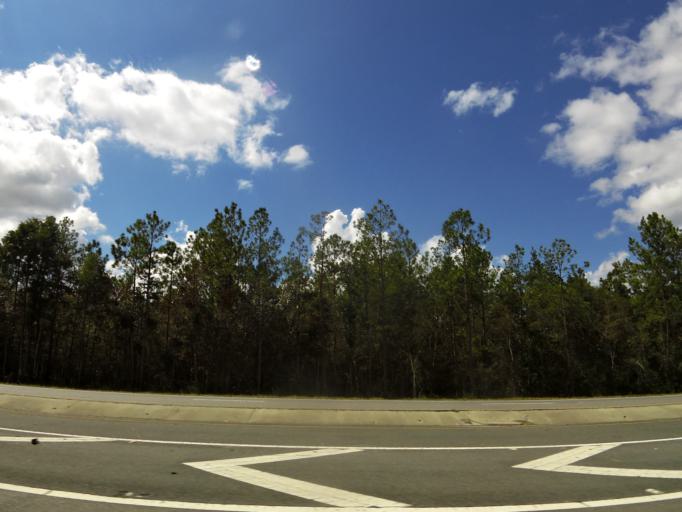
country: US
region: Georgia
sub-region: Charlton County
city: Folkston
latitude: 30.7840
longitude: -81.9798
